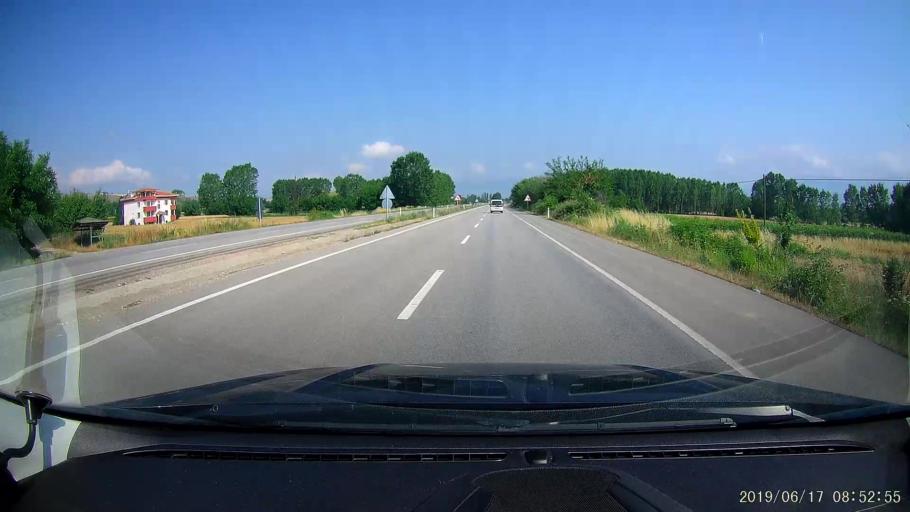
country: TR
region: Tokat
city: Erbaa
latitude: 40.7040
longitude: 36.4892
